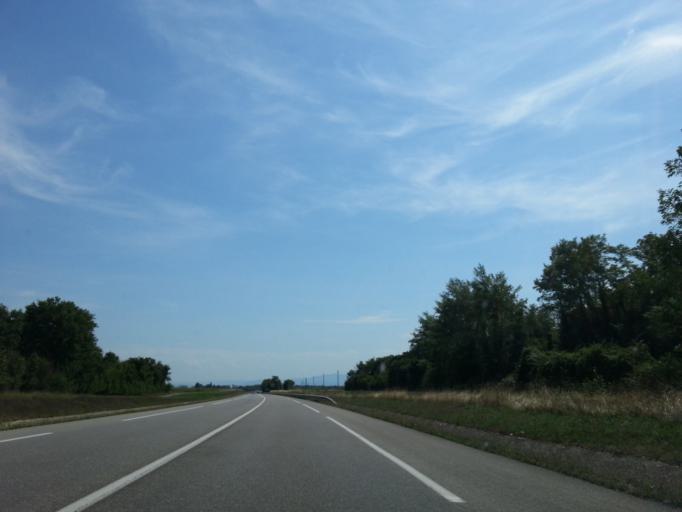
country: FR
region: Alsace
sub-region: Departement du Haut-Rhin
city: Wolfgantzen
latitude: 48.0353
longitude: 7.4875
